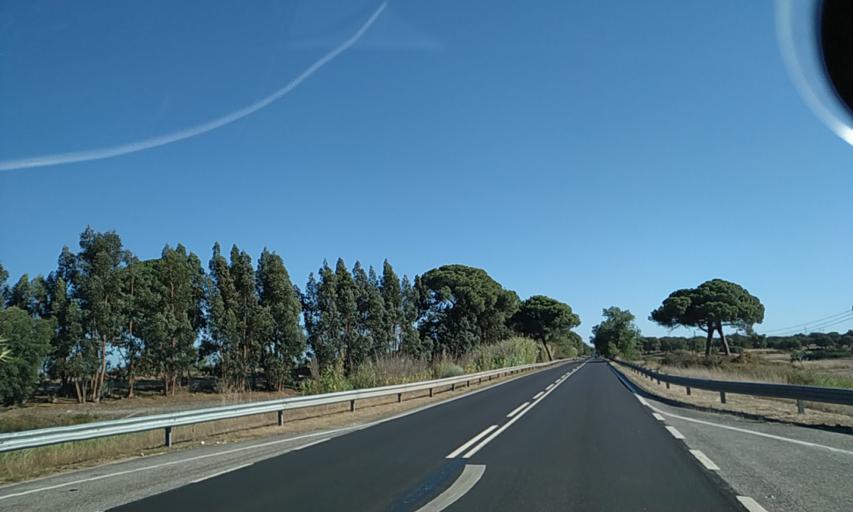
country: PT
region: Santarem
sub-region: Benavente
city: Samora Correia
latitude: 38.8638
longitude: -8.8812
